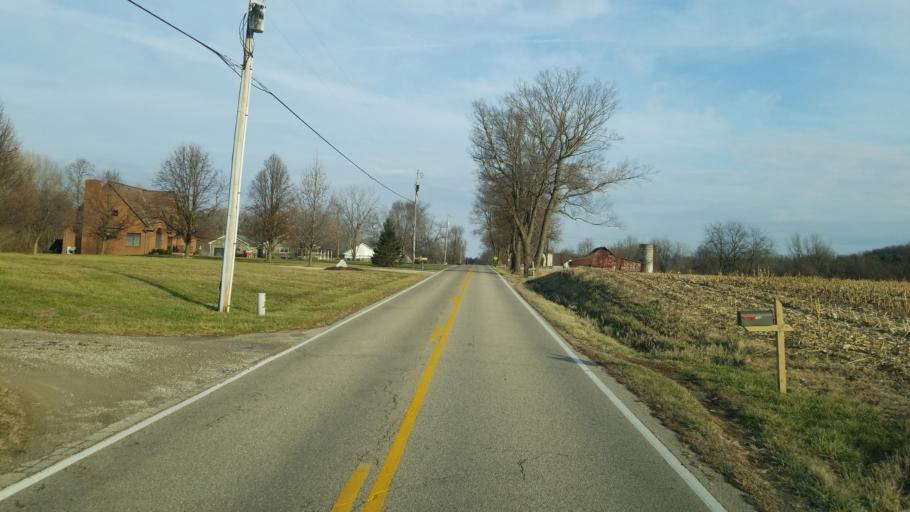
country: US
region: Ohio
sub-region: Ross County
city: Kingston
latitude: 39.4173
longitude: -82.9403
